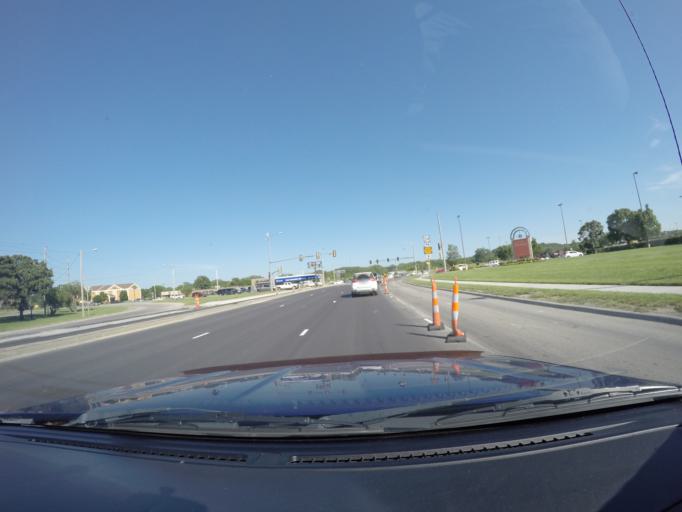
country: US
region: Kansas
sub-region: Riley County
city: Manhattan
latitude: 39.1800
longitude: -96.5569
